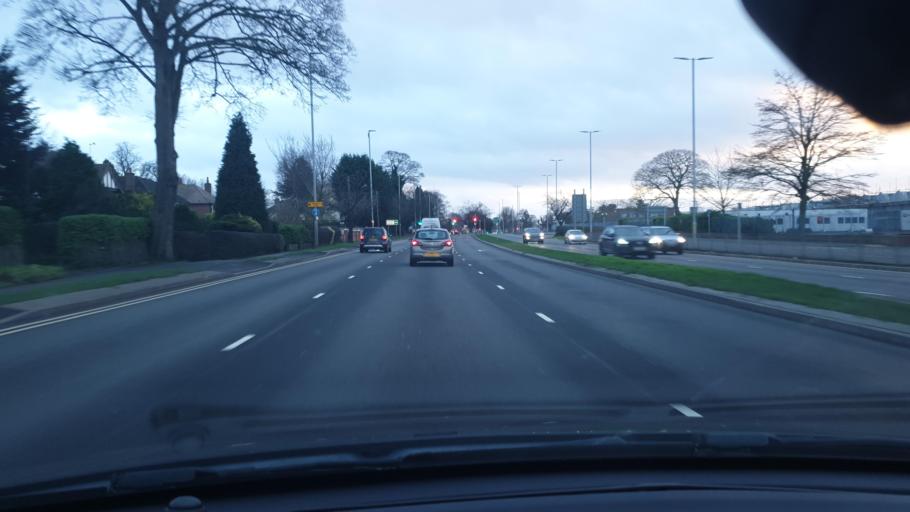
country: GB
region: England
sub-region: Staffordshire
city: Featherstone
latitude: 52.6337
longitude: -2.1249
